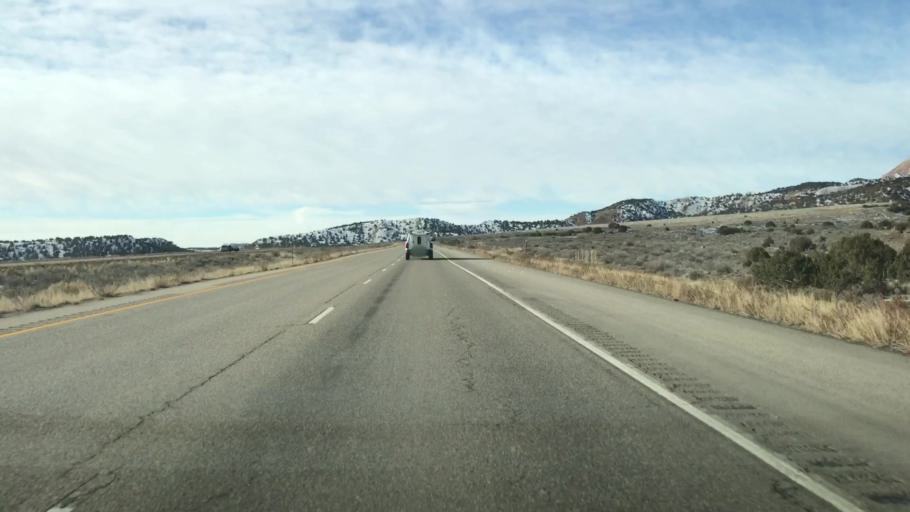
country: US
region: Colorado
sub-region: Garfield County
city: Parachute
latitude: 39.3870
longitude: -108.1437
